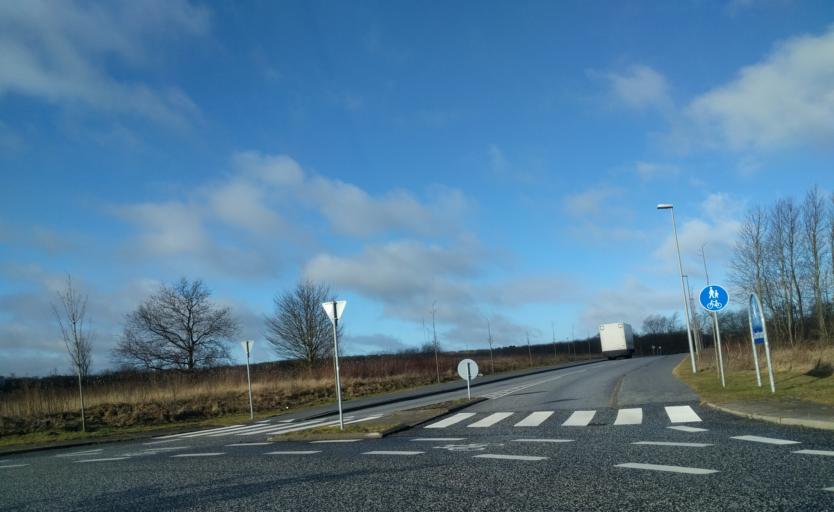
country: DK
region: North Denmark
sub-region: Alborg Kommune
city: Svenstrup
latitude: 56.9993
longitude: 9.8680
